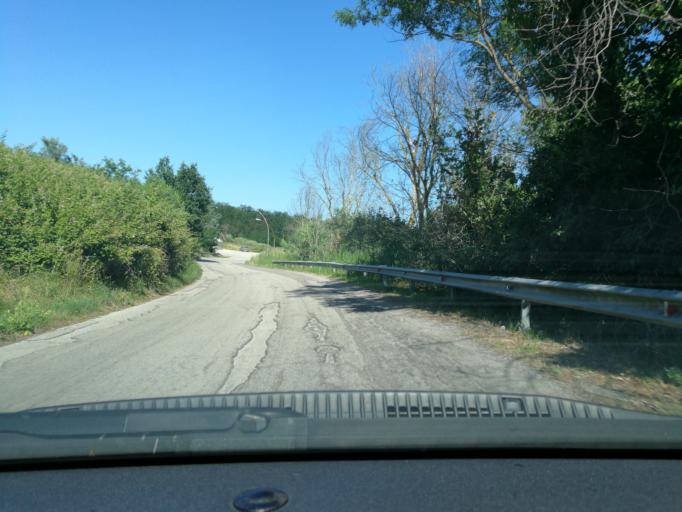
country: IT
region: Abruzzo
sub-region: Provincia di Chieti
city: Vasto
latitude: 42.1661
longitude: 14.6969
